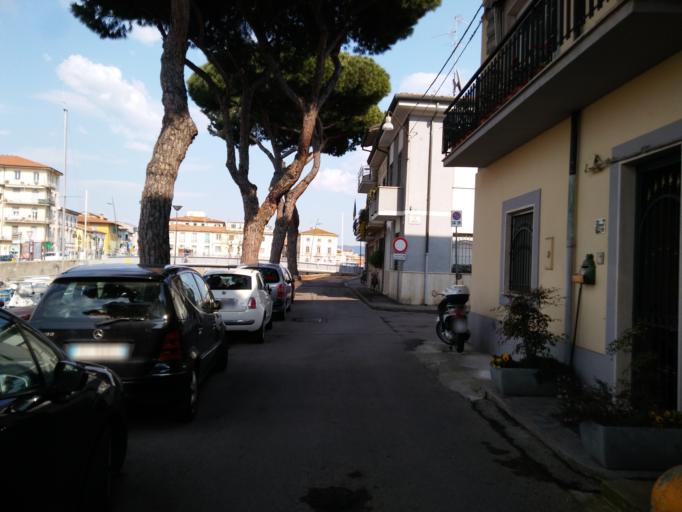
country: IT
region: Tuscany
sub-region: Provincia di Lucca
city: Viareggio
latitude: 43.8652
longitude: 10.2492
